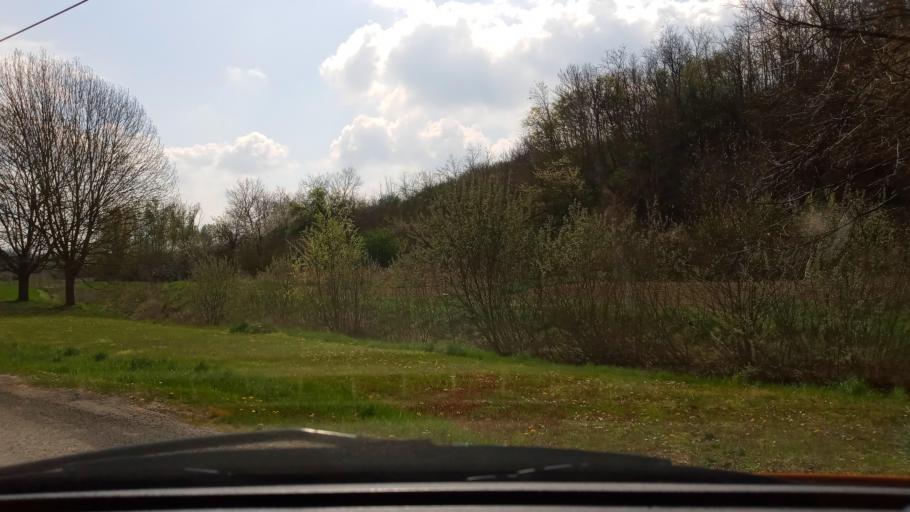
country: HU
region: Baranya
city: Boly
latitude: 46.0754
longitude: 18.5087
